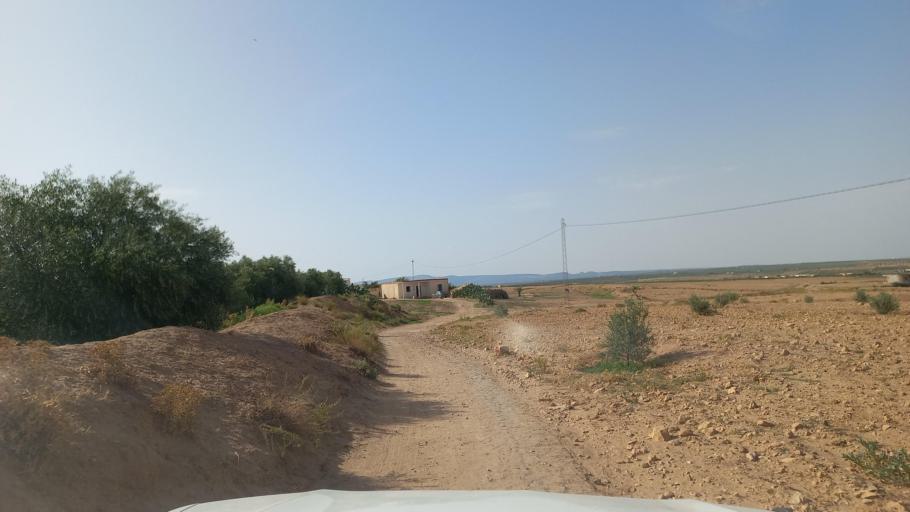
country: TN
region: Al Qasrayn
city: Kasserine
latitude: 35.3389
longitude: 8.8206
